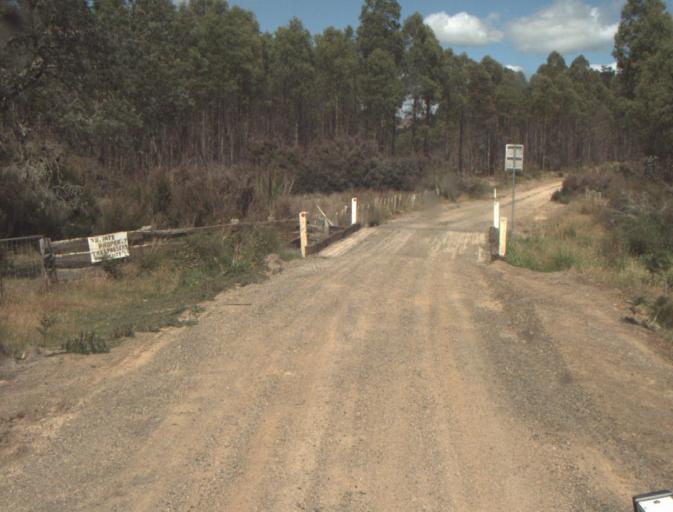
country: AU
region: Tasmania
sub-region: Dorset
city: Scottsdale
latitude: -41.4095
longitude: 147.5294
